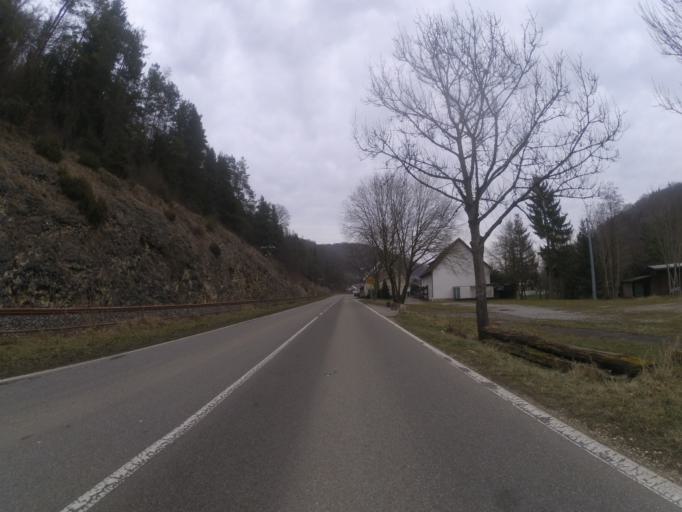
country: DE
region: Baden-Wuerttemberg
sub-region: Tuebingen Region
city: Schelklingen
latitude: 48.3661
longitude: 9.7069
